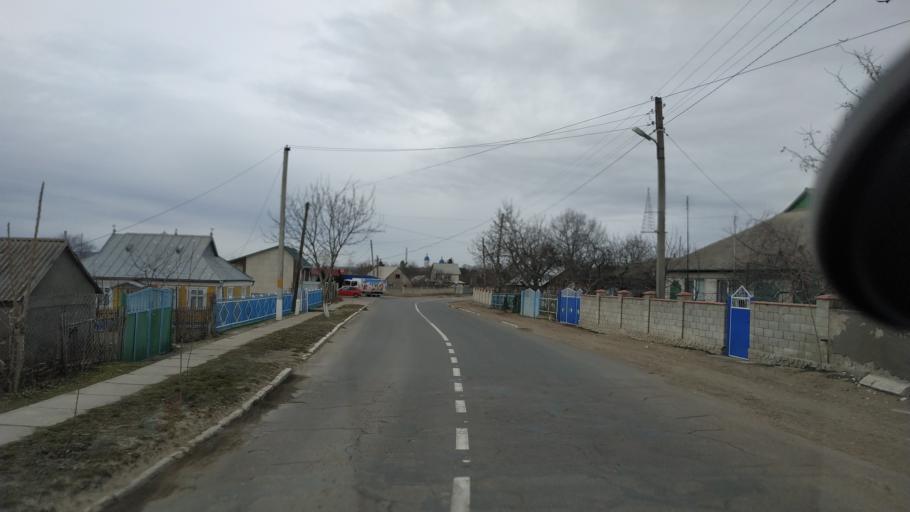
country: MD
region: Telenesti
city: Cocieri
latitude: 47.3042
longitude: 29.1128
